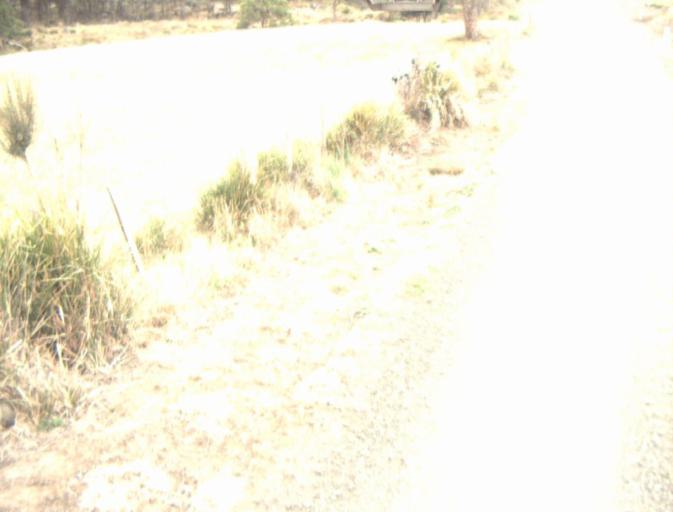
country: AU
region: Tasmania
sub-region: Dorset
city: Scottsdale
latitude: -41.4633
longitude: 147.5711
